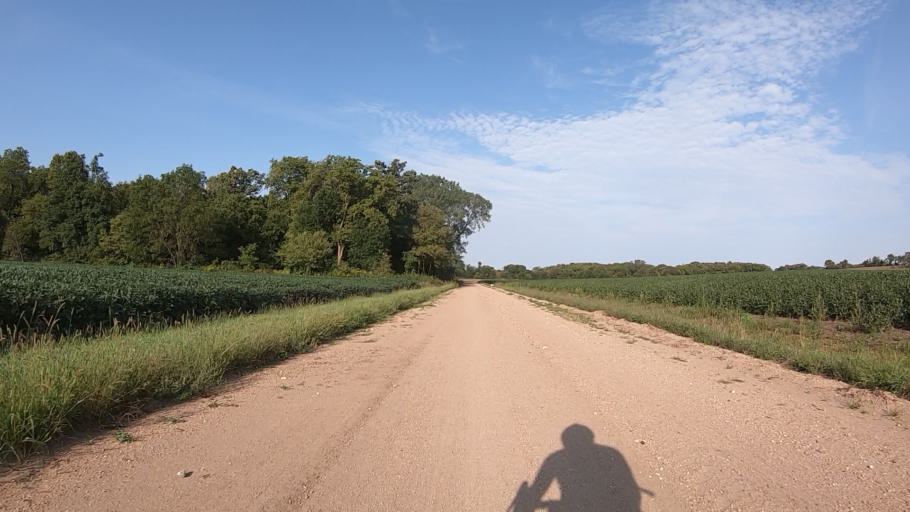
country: US
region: Kansas
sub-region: Marshall County
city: Blue Rapids
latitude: 39.6570
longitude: -96.8795
